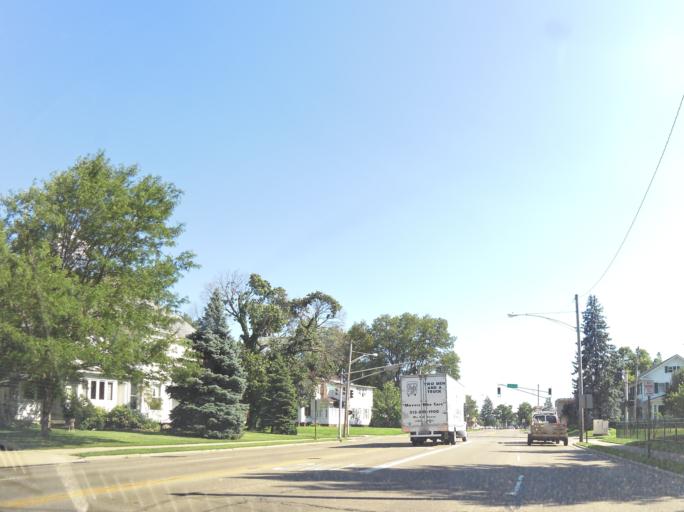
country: US
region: Ohio
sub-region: Greene County
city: Fairborn
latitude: 39.8243
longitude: -84.0209
